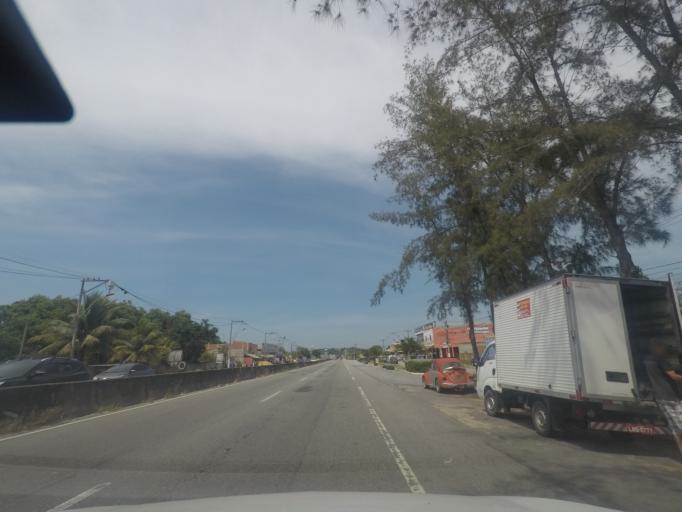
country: BR
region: Rio de Janeiro
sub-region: Marica
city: Marica
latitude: -22.9258
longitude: -42.8653
